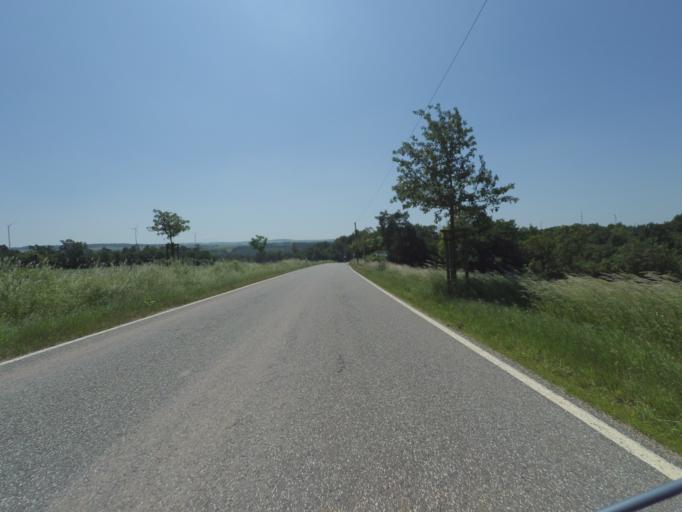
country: DE
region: Rheinland-Pfalz
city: Lahr
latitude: 50.1179
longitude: 7.3635
